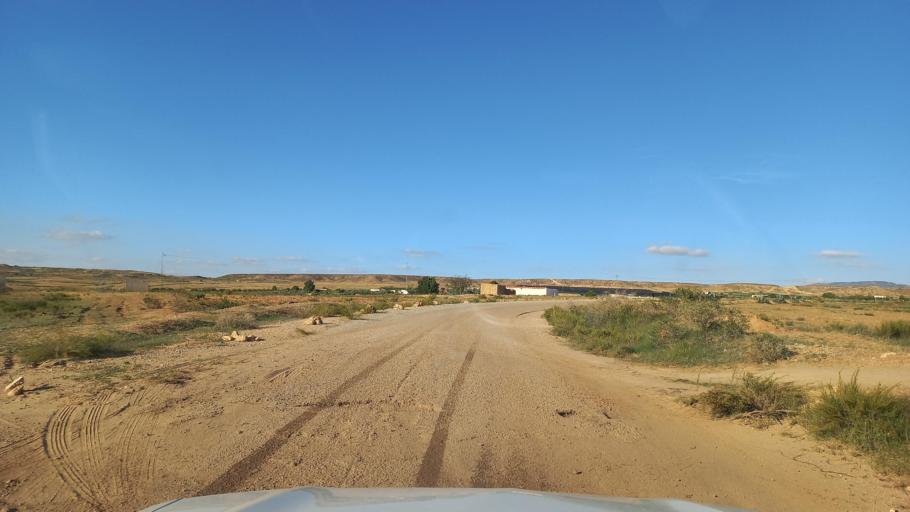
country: TN
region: Al Qasrayn
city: Sbiba
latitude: 35.3400
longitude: 9.1196
